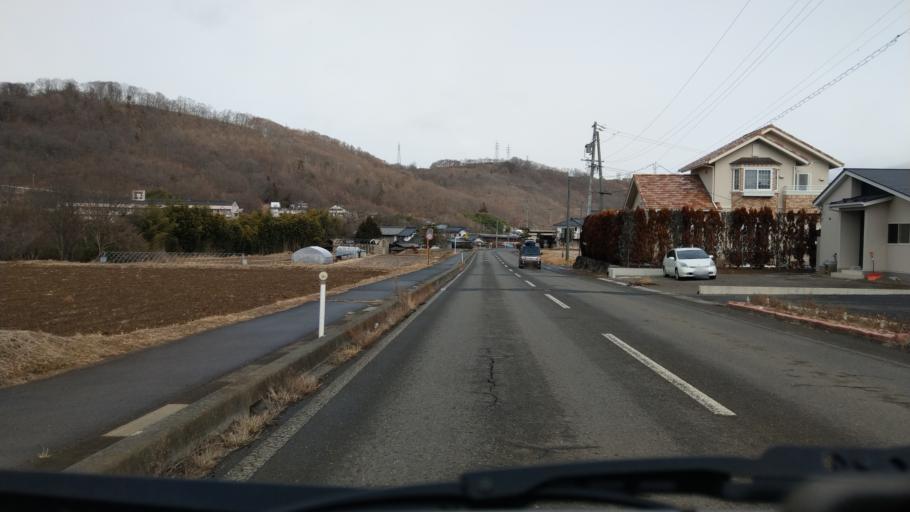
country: JP
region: Nagano
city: Kamimaruko
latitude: 36.3221
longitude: 138.3446
